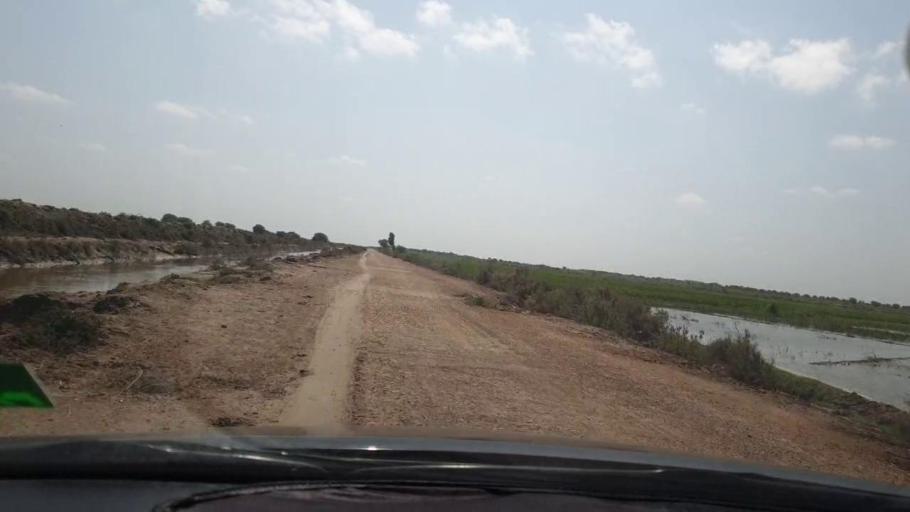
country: PK
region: Sindh
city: Tando Bago
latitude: 24.8400
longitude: 69.0456
